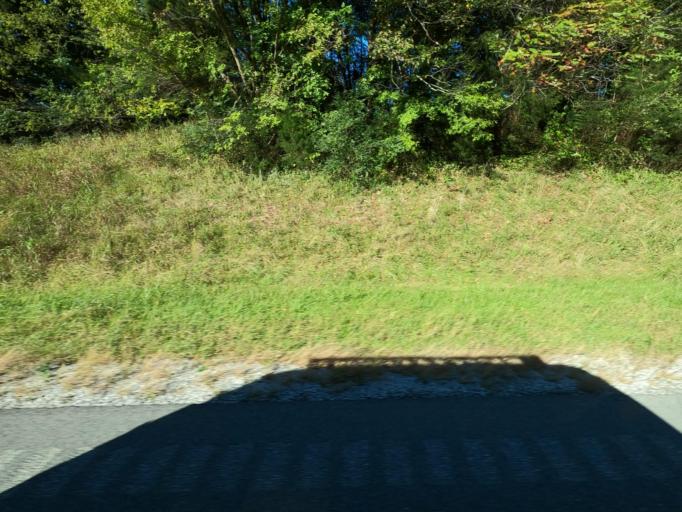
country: US
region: Tennessee
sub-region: Rutherford County
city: Plainview
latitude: 35.6104
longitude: -86.2399
